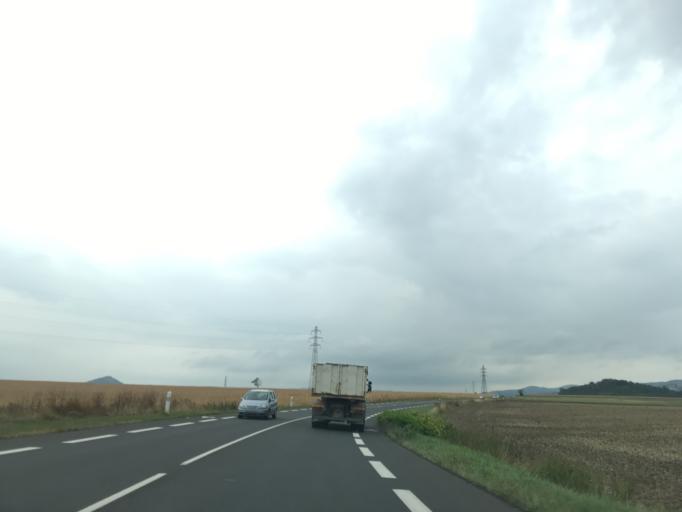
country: FR
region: Auvergne
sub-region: Departement du Puy-de-Dome
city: Perignat-sur-Allier
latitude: 45.7290
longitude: 3.2506
